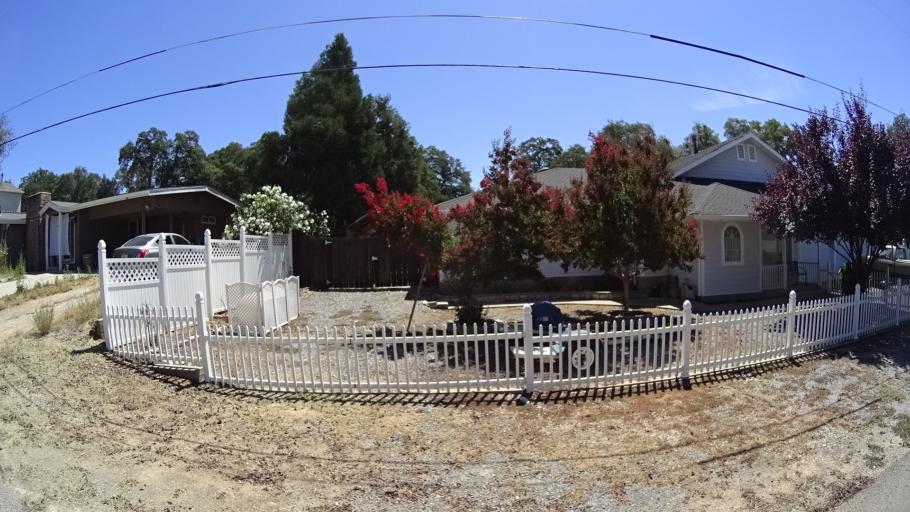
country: US
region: California
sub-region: Calaveras County
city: Angels Camp
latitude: 38.0830
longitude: -120.5630
